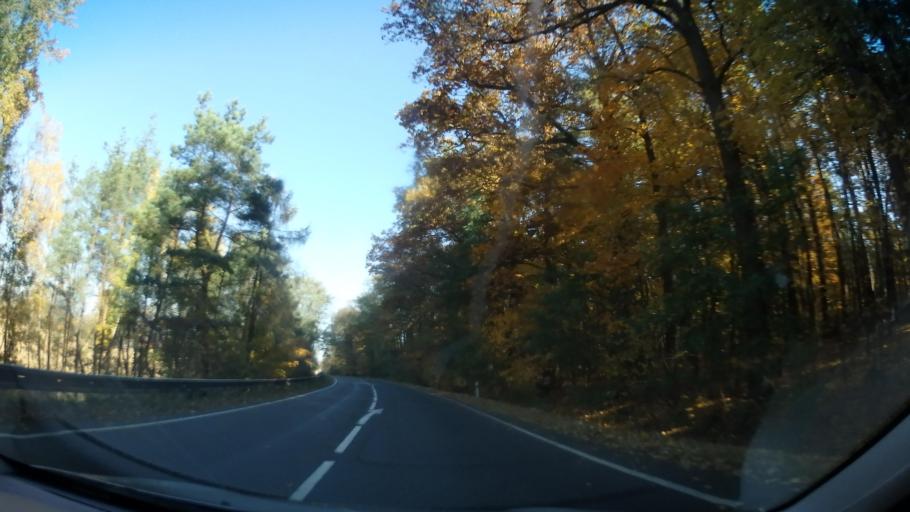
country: CZ
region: Kralovehradecky
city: Trebechovice pod Orebem
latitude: 50.2076
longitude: 16.0226
